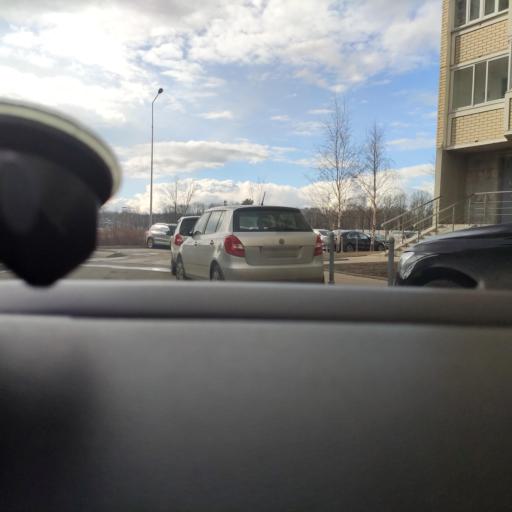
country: RU
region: Moscow
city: Novo-Peredelkino
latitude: 55.6446
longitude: 37.3275
